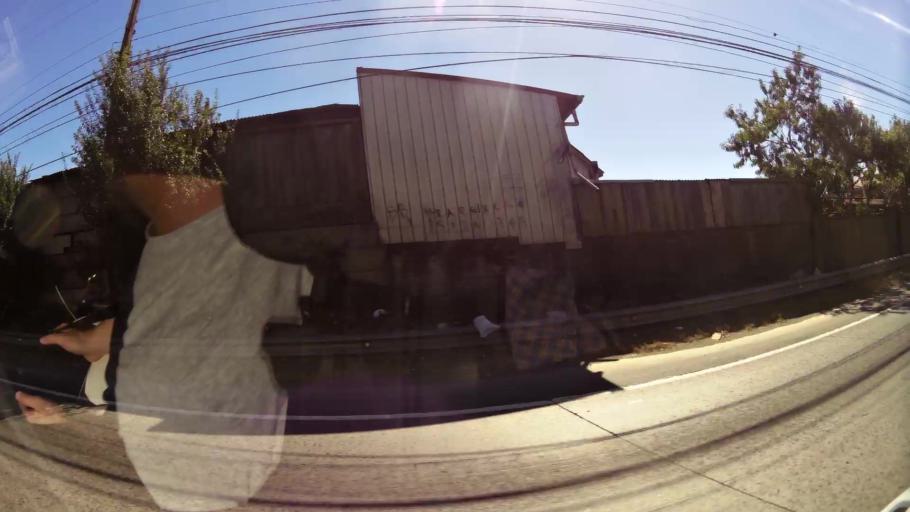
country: CL
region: Biobio
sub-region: Provincia de Concepcion
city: Concepcion
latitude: -36.7992
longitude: -73.0258
